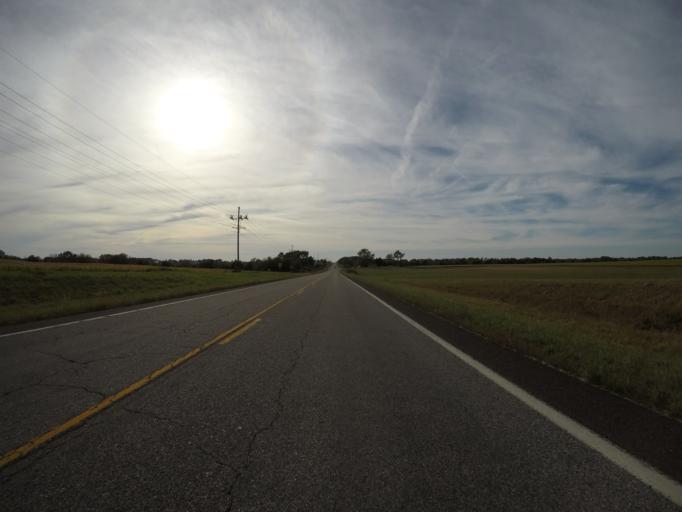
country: US
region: Kansas
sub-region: Franklin County
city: Wellsville
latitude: 38.7679
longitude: -95.0704
